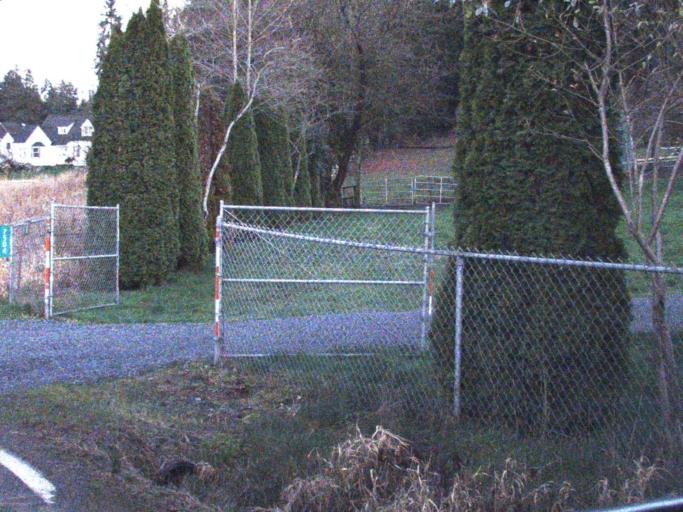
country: US
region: Washington
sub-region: Snohomish County
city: Silver Firs
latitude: 47.8824
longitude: -122.1303
